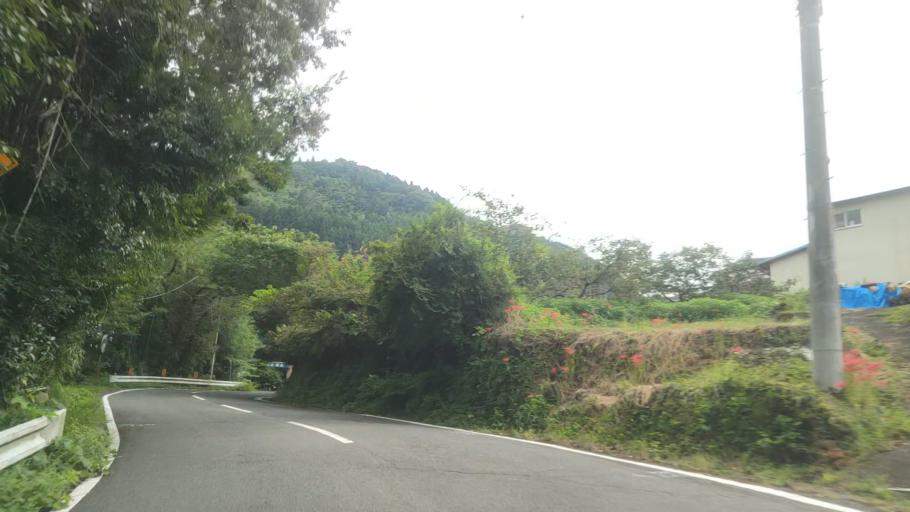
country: JP
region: Wakayama
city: Koya
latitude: 34.2597
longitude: 135.5467
